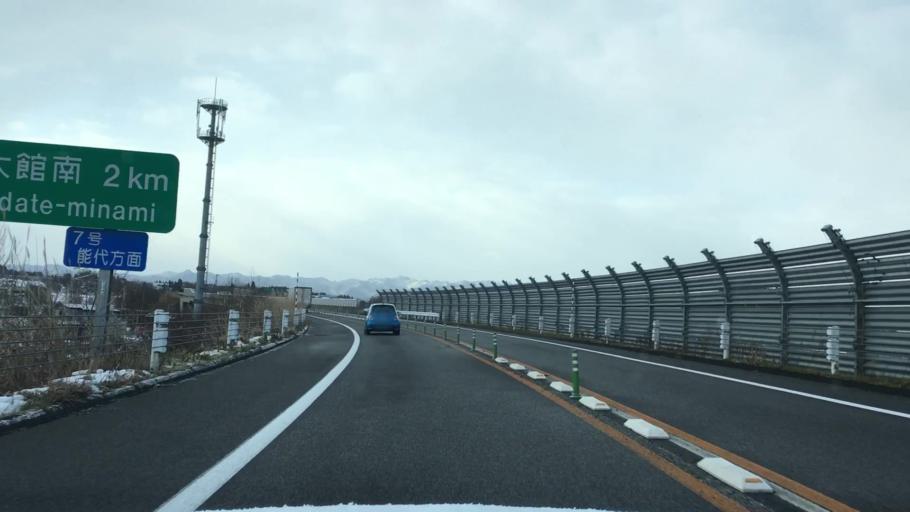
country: JP
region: Akita
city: Odate
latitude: 40.2873
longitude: 140.5418
